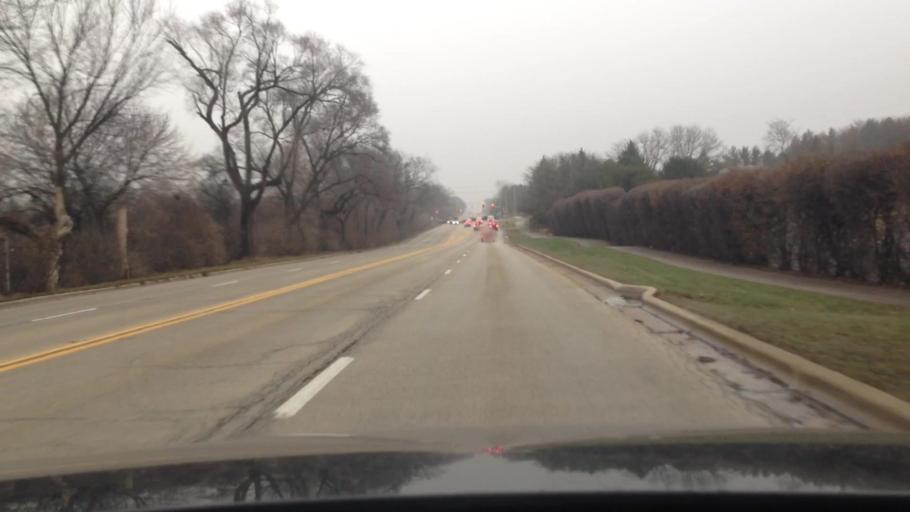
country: US
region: Illinois
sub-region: DuPage County
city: Oakbrook Terrace
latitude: 41.8315
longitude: -87.9762
